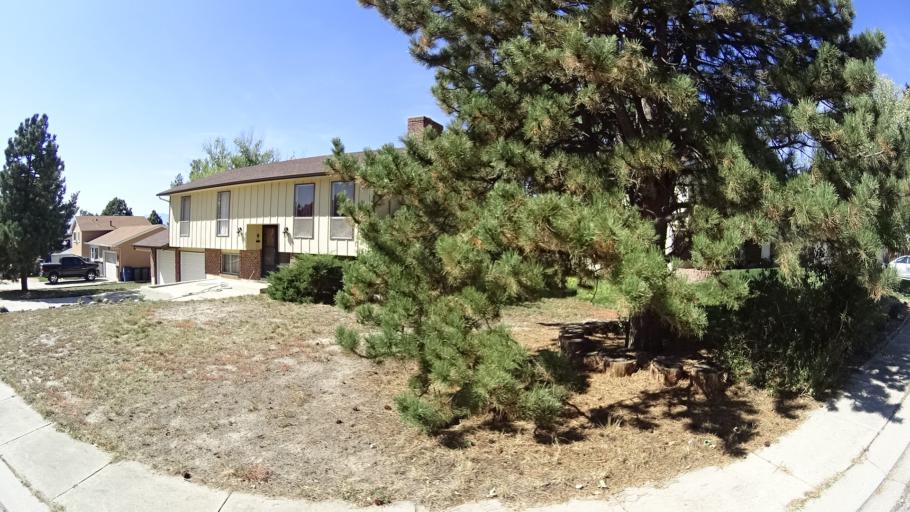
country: US
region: Colorado
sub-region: El Paso County
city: Cimarron Hills
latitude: 38.9147
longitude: -104.7657
